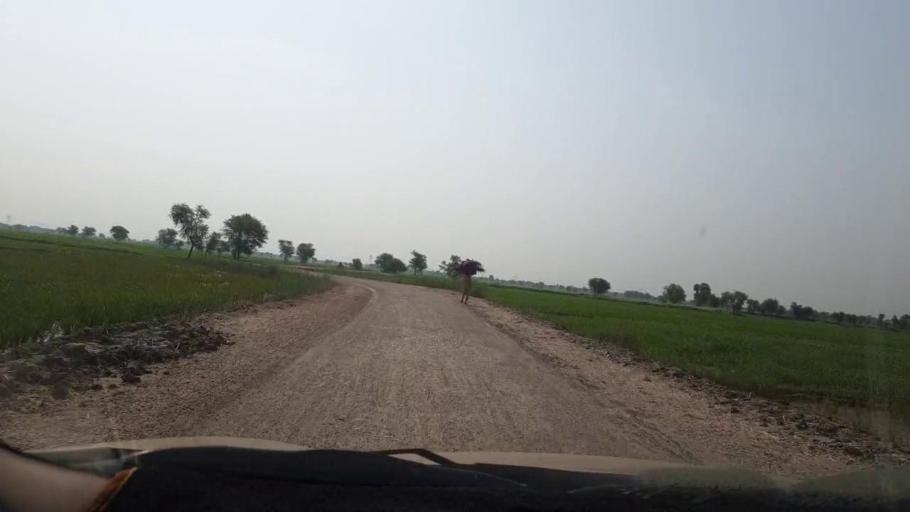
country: PK
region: Sindh
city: Goth Garelo
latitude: 27.4454
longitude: 68.0365
